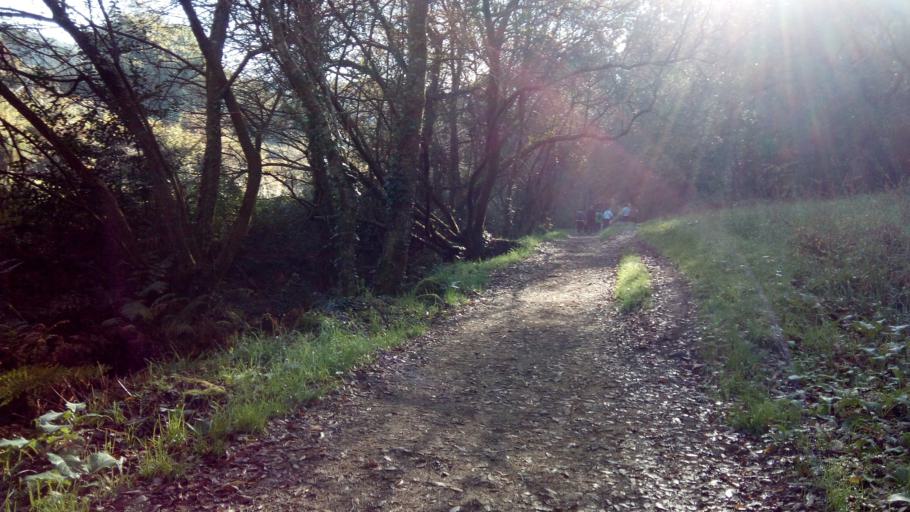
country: ES
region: Galicia
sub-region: Provincia de Pontevedra
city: Meis
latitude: 42.4833
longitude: -8.7426
